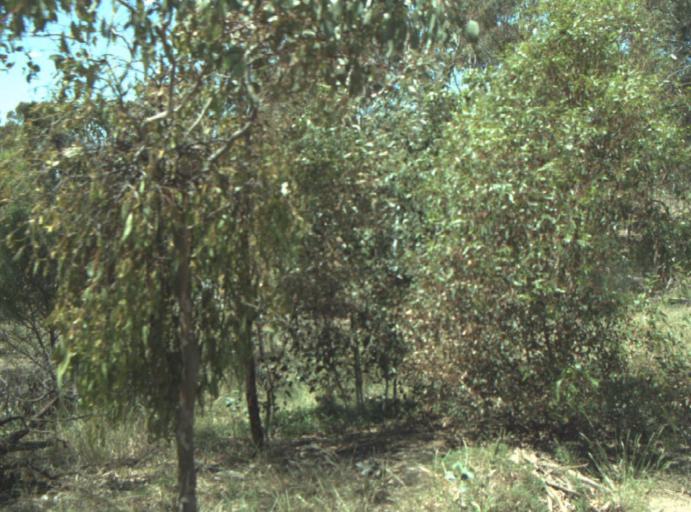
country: AU
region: Victoria
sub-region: Moorabool
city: Bacchus Marsh
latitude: -37.8360
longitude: 144.2878
